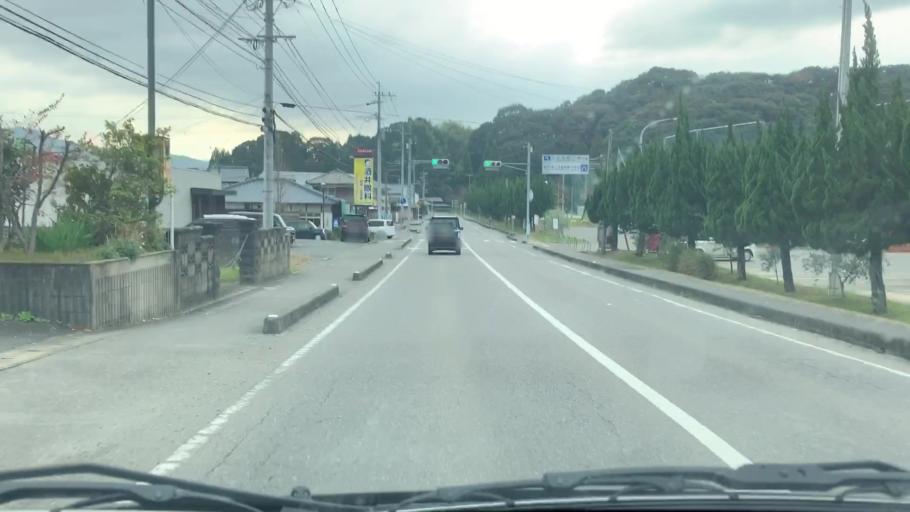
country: JP
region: Saga Prefecture
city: Takeocho-takeo
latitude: 33.1935
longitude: 130.0307
